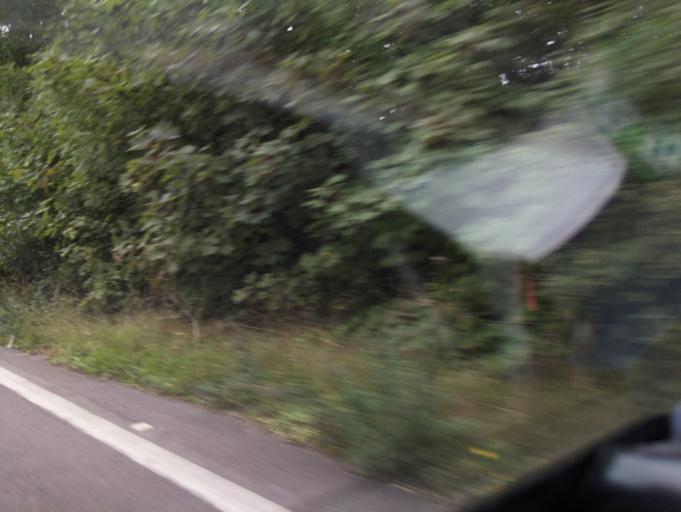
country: GB
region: England
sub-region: Devon
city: Kingskerswell
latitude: 50.4846
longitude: -3.5732
